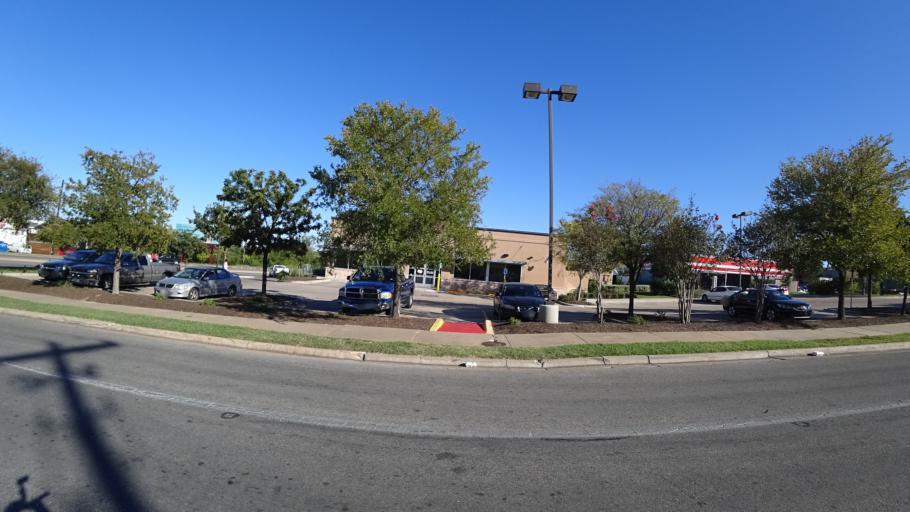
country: US
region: Texas
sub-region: Travis County
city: Austin
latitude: 30.2397
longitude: -97.7273
